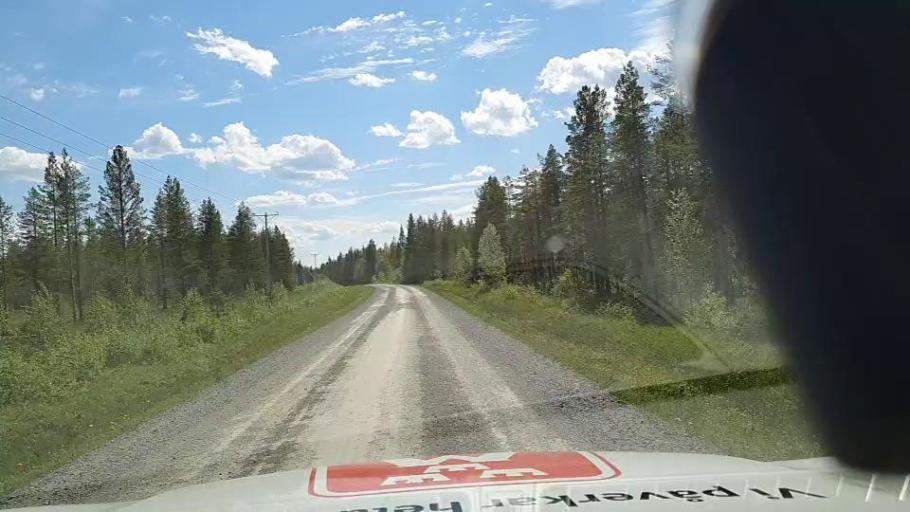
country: SE
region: Jaemtland
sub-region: Stroemsunds Kommun
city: Stroemsund
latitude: 64.4621
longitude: 15.5924
